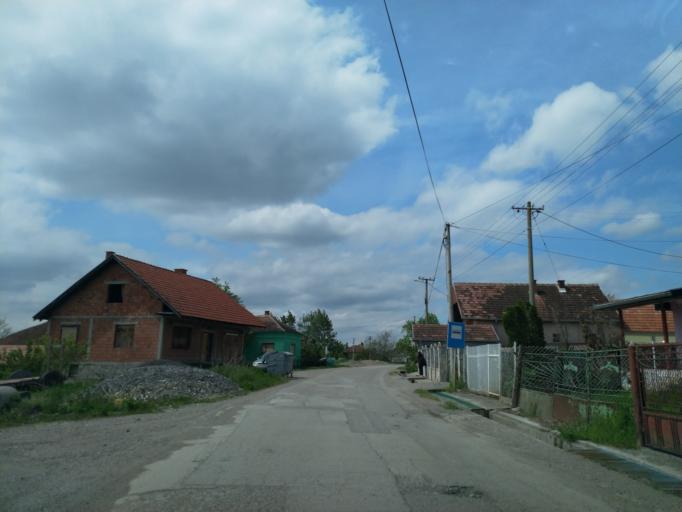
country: RS
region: Central Serbia
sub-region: Pomoravski Okrug
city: Paracin
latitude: 43.9386
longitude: 21.4911
